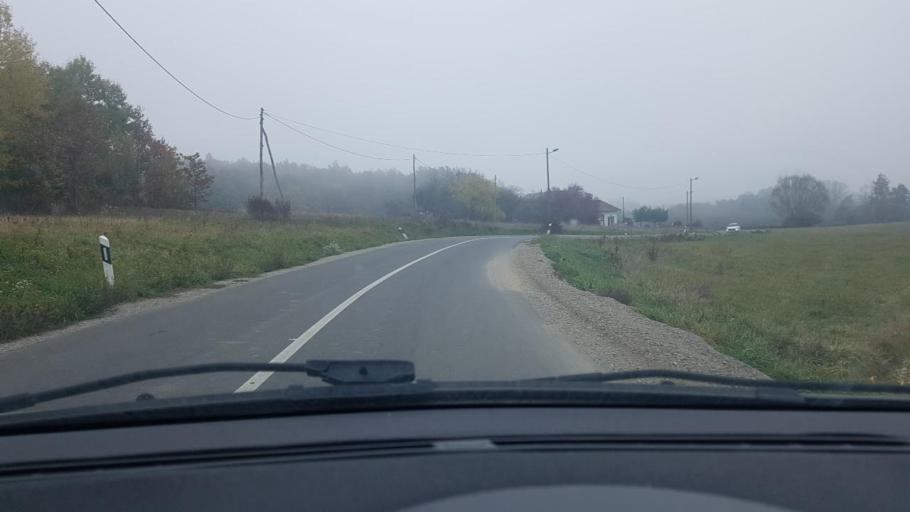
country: HR
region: Varazdinska
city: Ivanec
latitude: 46.1388
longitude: 16.1728
